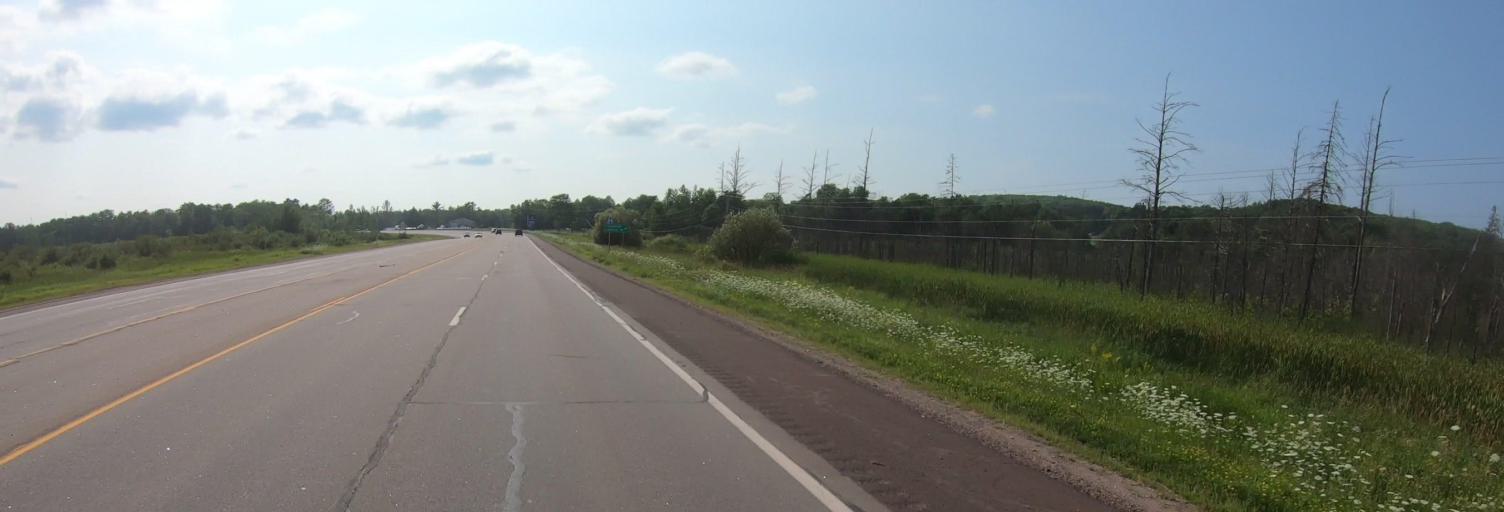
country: US
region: Michigan
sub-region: Gogebic County
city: Bessemer
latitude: 46.4778
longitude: -90.1007
